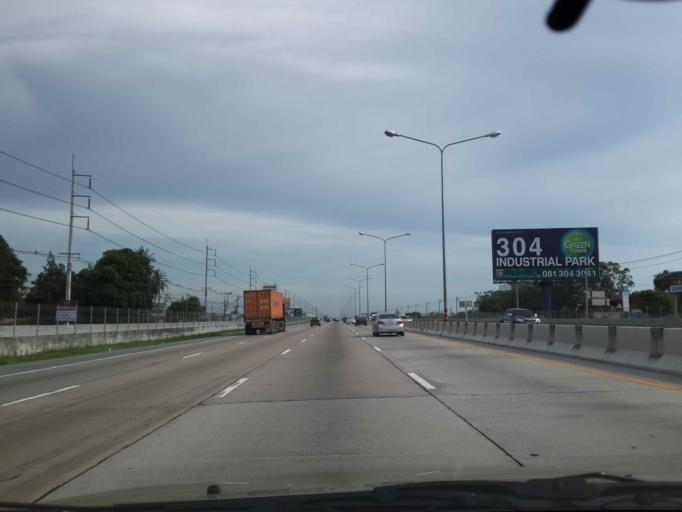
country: TH
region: Chon Buri
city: Si Racha
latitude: 13.1683
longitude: 100.9912
